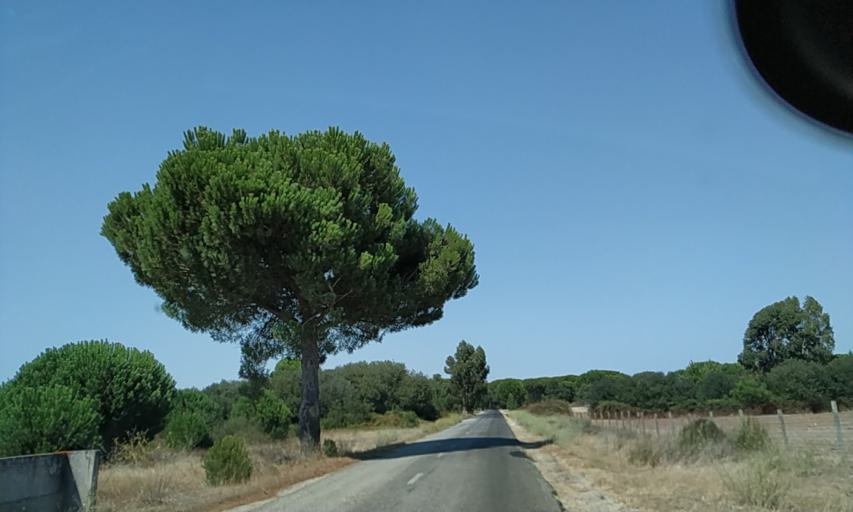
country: PT
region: Santarem
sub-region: Benavente
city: Poceirao
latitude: 38.7320
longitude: -8.7010
